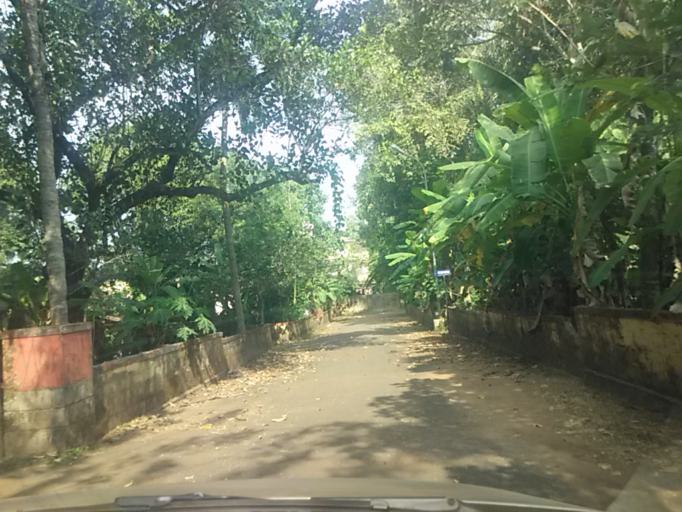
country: IN
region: Kerala
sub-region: Kozhikode
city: Mavoor
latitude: 11.3170
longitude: 75.9316
